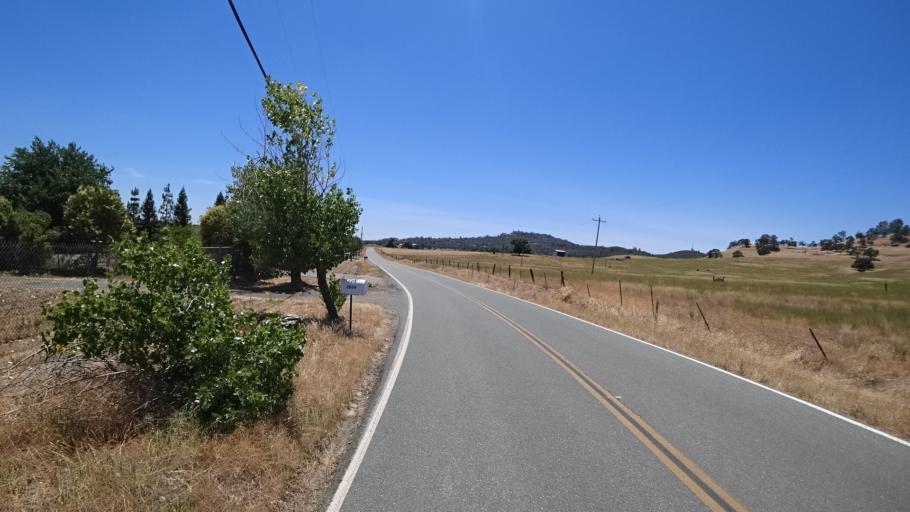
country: US
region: California
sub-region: Calaveras County
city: Valley Springs
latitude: 38.2231
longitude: -120.8224
